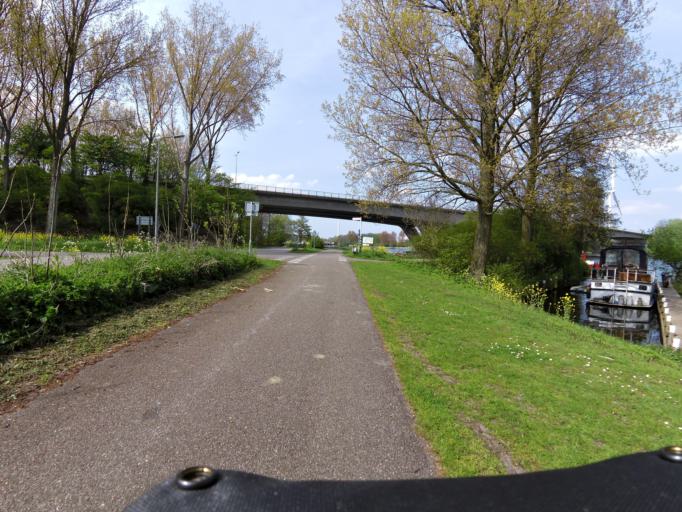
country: NL
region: South Holland
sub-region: Gemeente Brielle
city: Brielle
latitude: 51.8978
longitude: 4.2066
